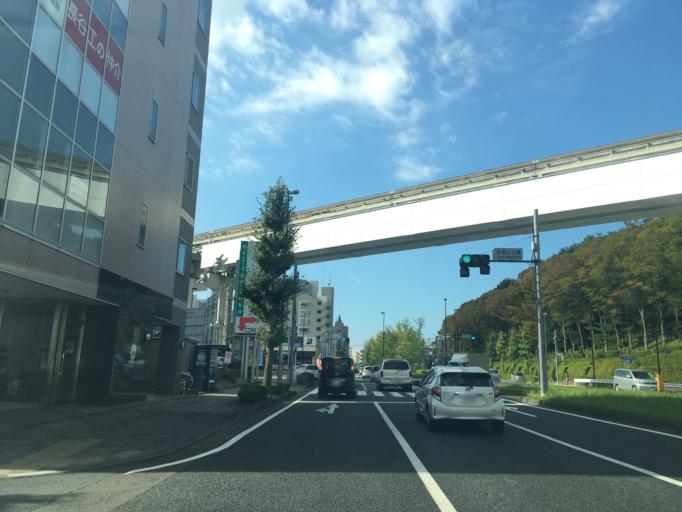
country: JP
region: Tokyo
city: Hino
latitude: 35.6265
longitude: 139.4243
